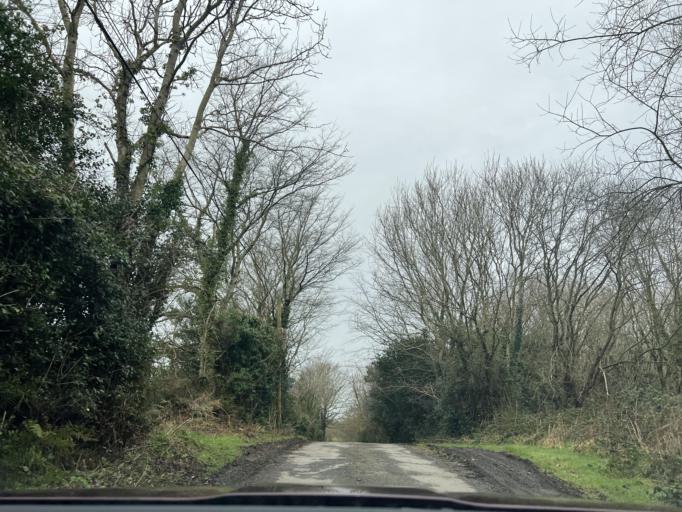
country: IE
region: Leinster
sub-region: Loch Garman
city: Castlebridge
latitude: 52.3840
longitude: -6.5517
